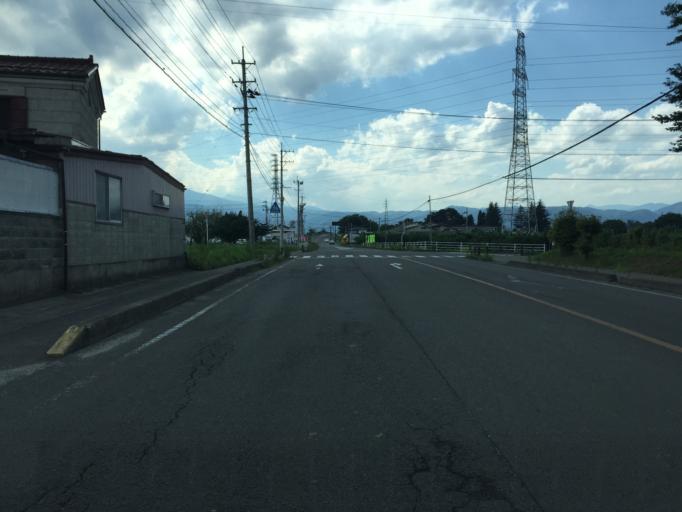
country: JP
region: Fukushima
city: Fukushima-shi
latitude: 37.7492
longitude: 140.4249
